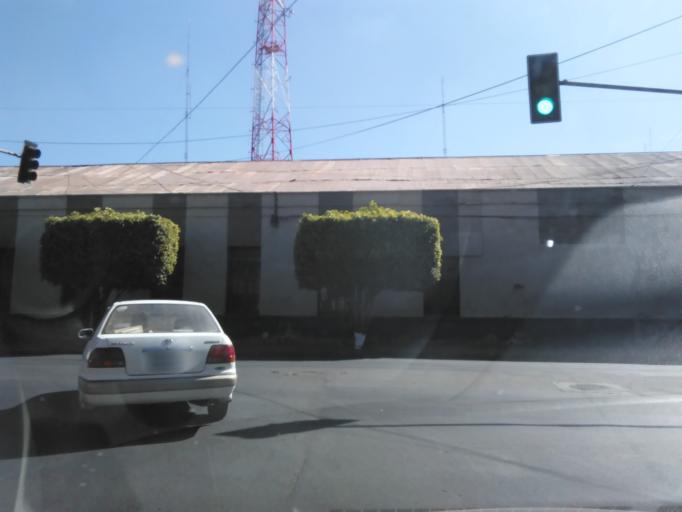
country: BO
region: Cochabamba
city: Cochabamba
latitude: -17.3937
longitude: -66.1649
